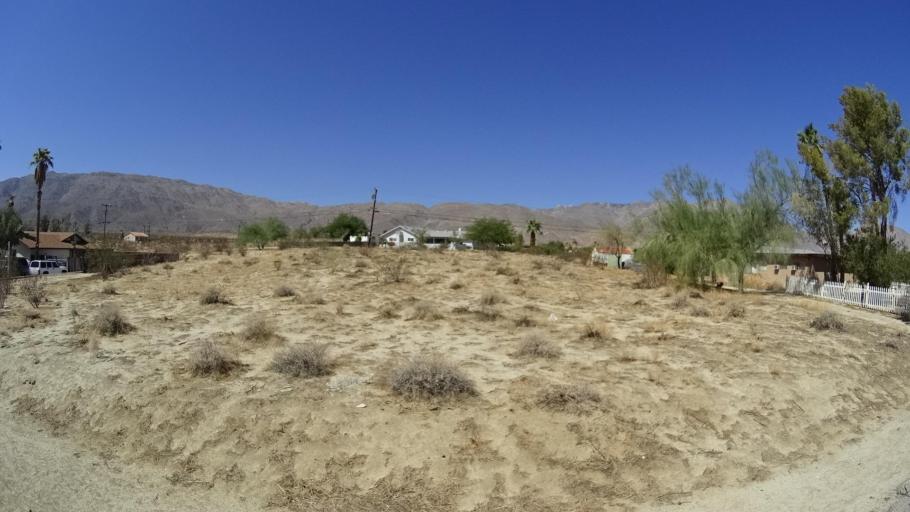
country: US
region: California
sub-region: San Diego County
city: Borrego Springs
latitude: 33.2294
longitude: -116.3722
